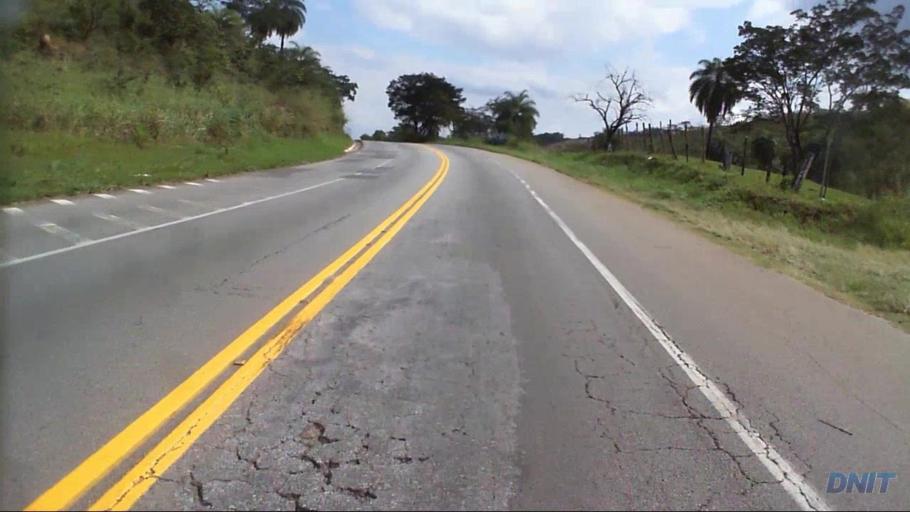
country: BR
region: Minas Gerais
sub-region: Santa Luzia
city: Santa Luzia
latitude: -19.8100
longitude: -43.7933
